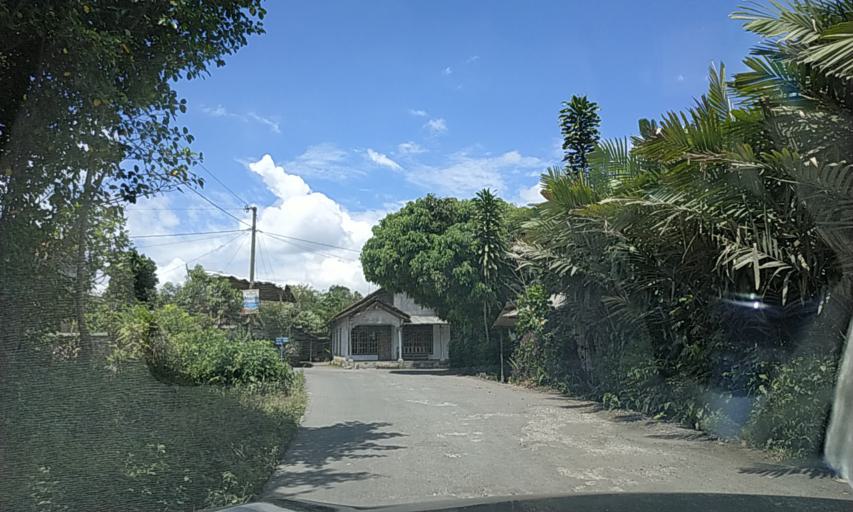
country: ID
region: Central Java
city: Muntilan
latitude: -7.6072
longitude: 110.3659
